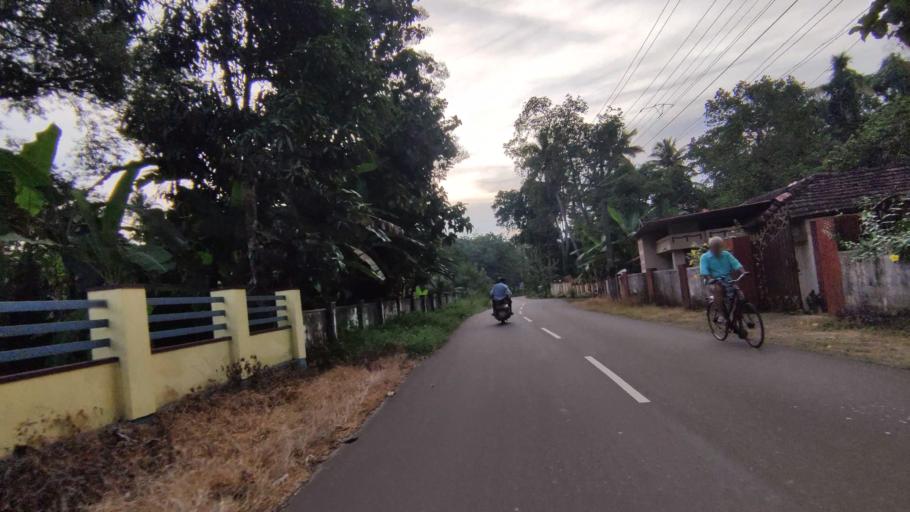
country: IN
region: Kerala
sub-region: Kottayam
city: Kottayam
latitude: 9.6372
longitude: 76.4950
